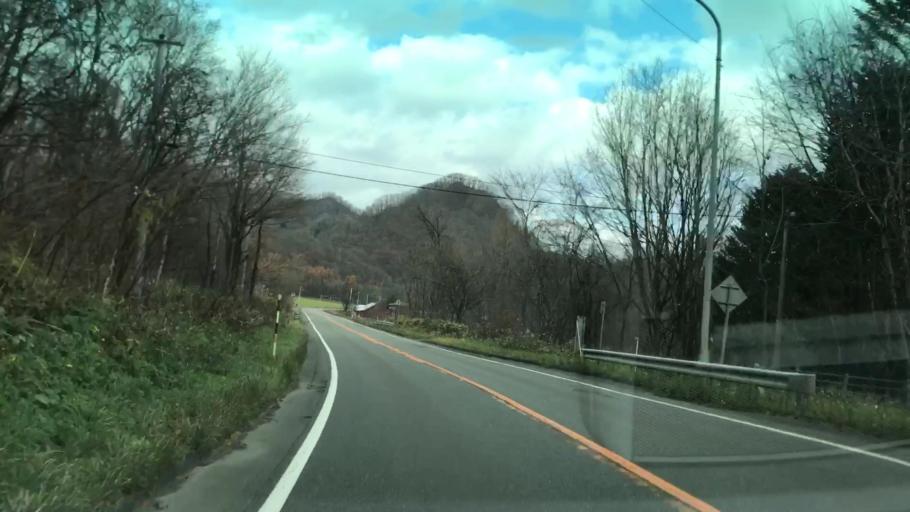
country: JP
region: Hokkaido
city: Shizunai-furukawacho
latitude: 42.8007
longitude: 142.3977
